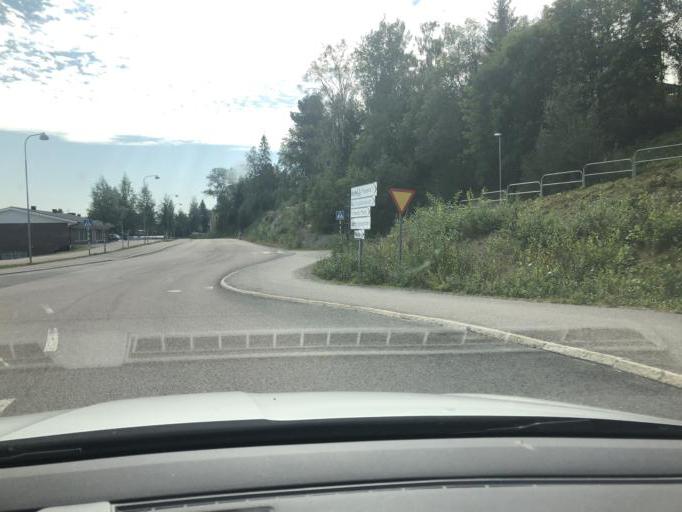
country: SE
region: Vaesternorrland
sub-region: Kramfors Kommun
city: Kramfors
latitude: 62.9278
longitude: 17.7785
